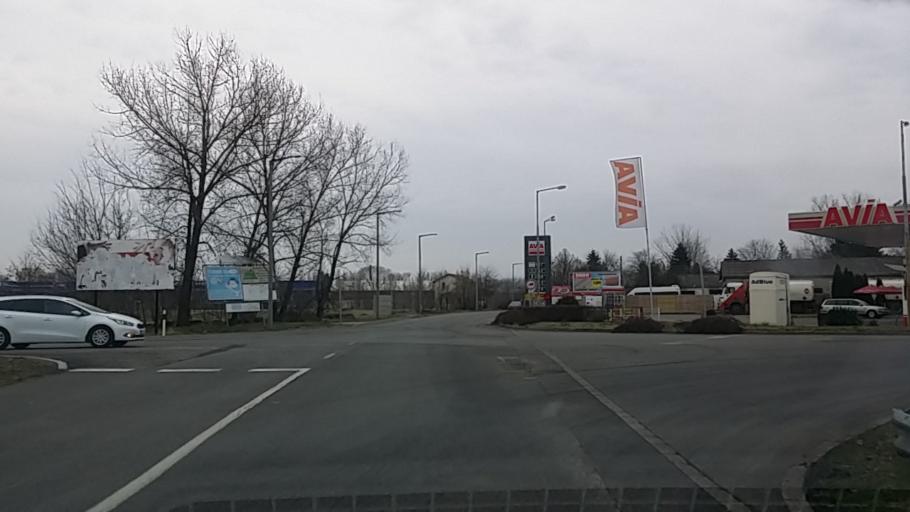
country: HU
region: Bacs-Kiskun
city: Baja
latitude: 46.1902
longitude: 18.9341
